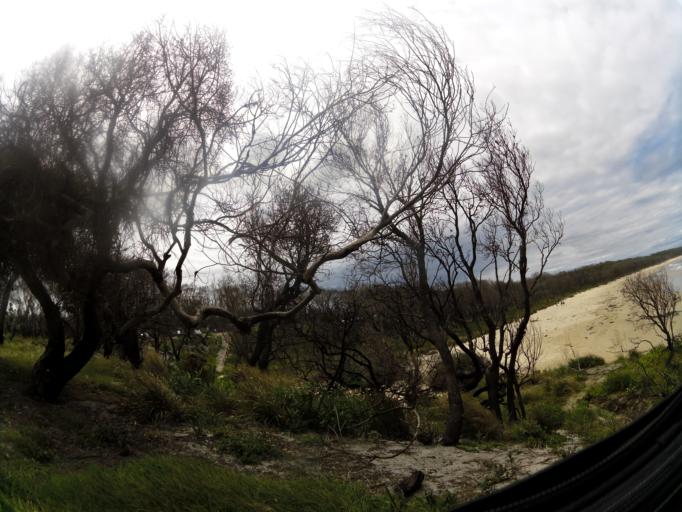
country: AU
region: Victoria
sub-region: East Gippsland
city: Lakes Entrance
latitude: -37.8003
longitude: 148.7423
